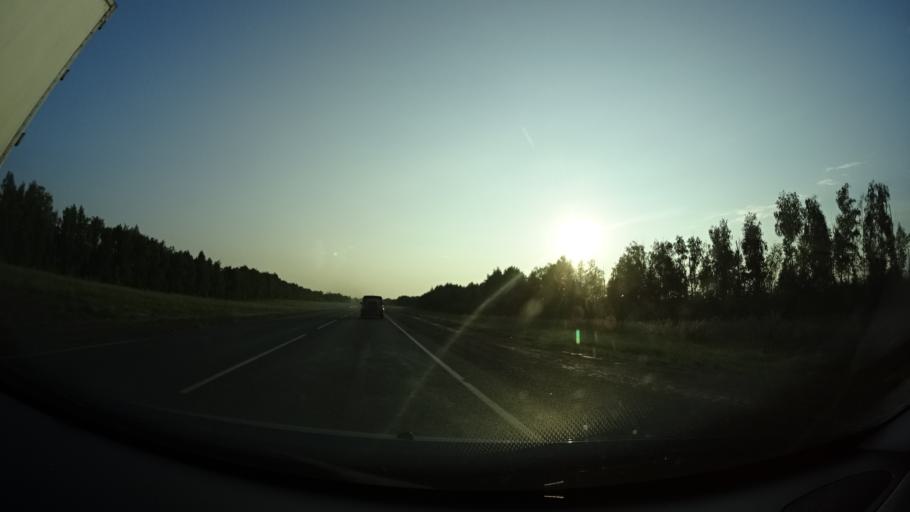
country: RU
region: Samara
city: Klyavlino
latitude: 54.0244
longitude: 51.8613
